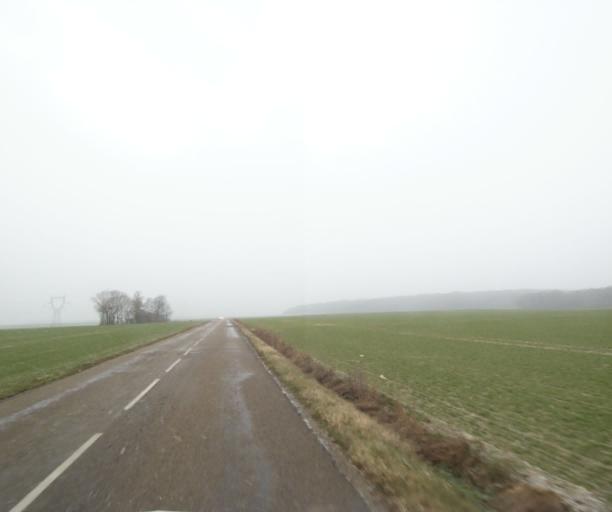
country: FR
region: Champagne-Ardenne
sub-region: Departement de la Haute-Marne
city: Bienville
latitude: 48.5209
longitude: 5.0332
